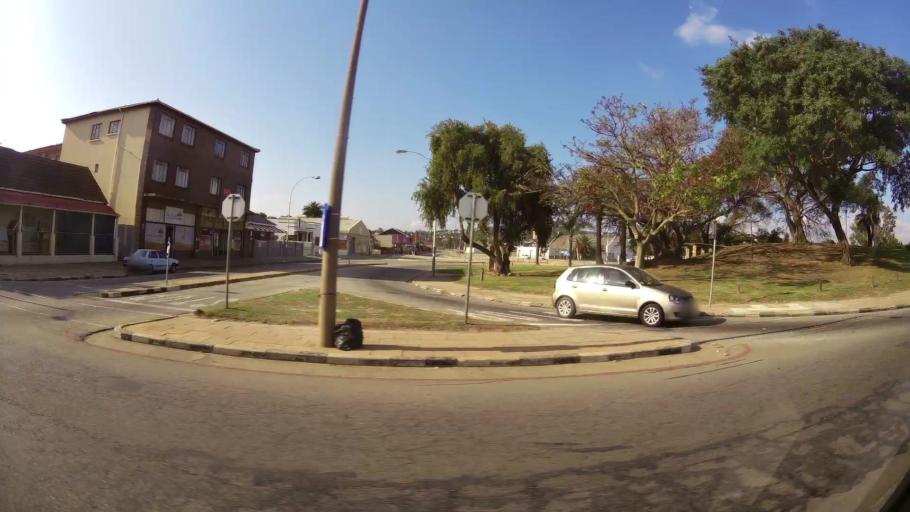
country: ZA
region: Eastern Cape
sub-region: Nelson Mandela Bay Metropolitan Municipality
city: Uitenhage
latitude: -33.7723
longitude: 25.4066
